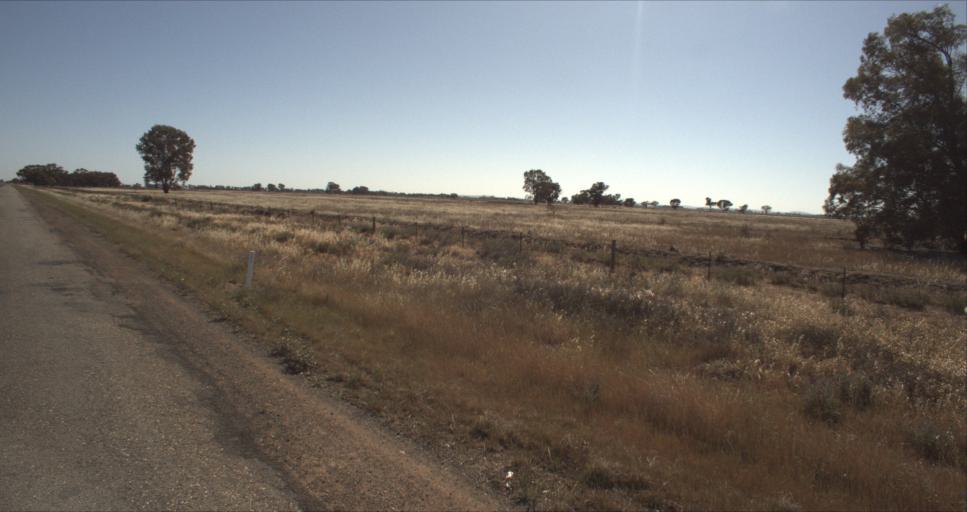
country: AU
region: New South Wales
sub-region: Leeton
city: Leeton
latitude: -34.5958
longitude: 146.2587
